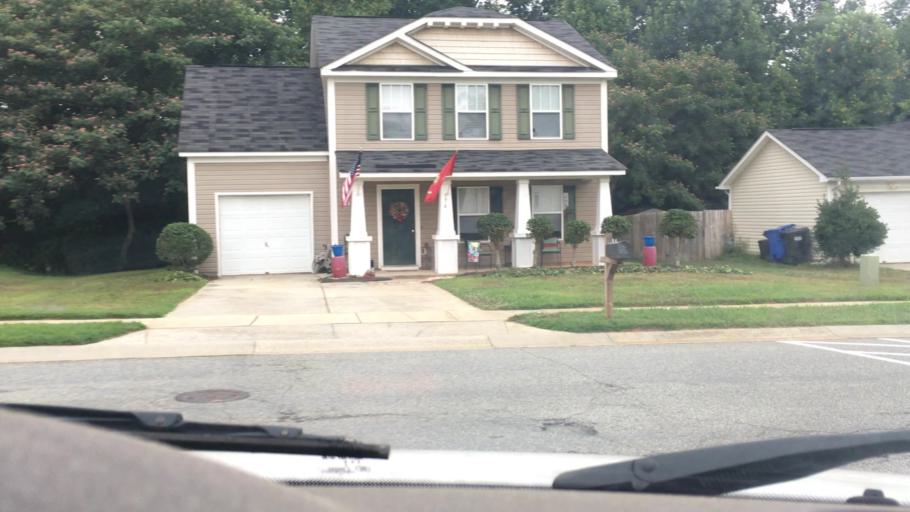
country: US
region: North Carolina
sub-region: Gaston County
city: Davidson
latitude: 35.5413
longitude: -80.8293
